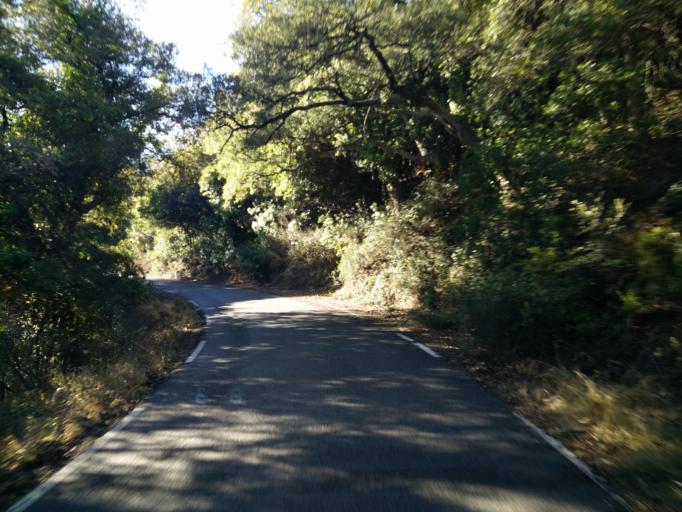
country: FR
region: Provence-Alpes-Cote d'Azur
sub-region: Departement du Var
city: Collobrieres
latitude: 43.2550
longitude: 6.3982
